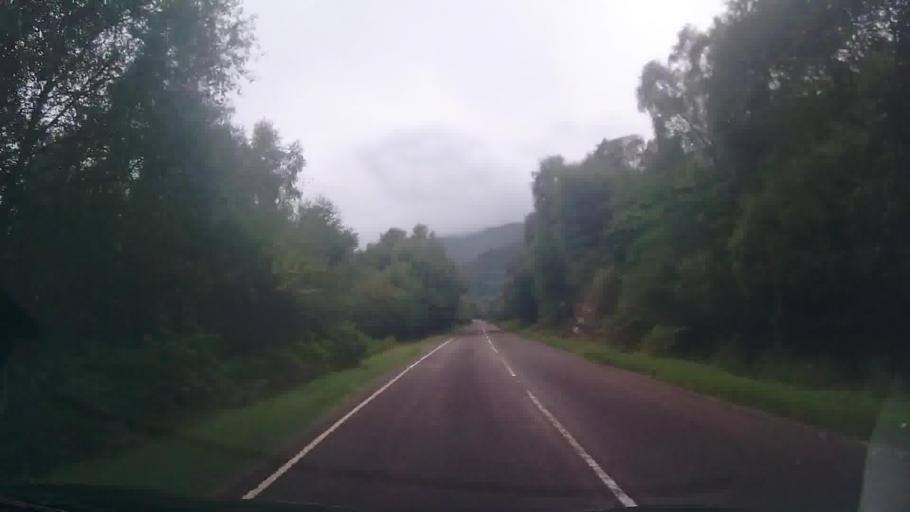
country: GB
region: Scotland
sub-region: Highland
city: Fort William
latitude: 56.6972
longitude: -5.3235
